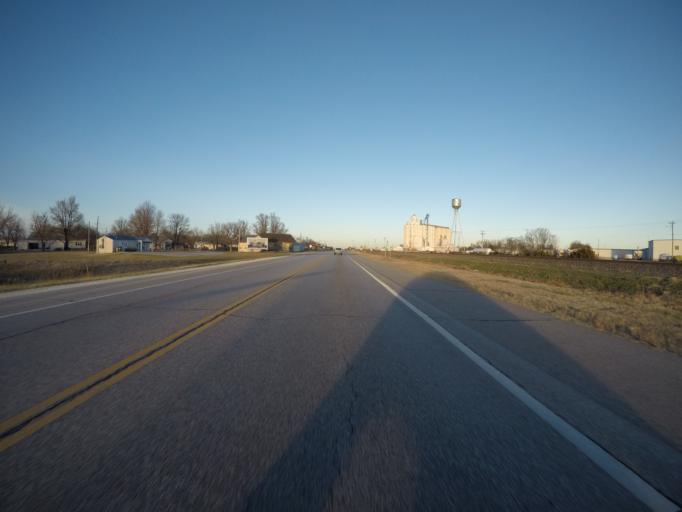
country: US
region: Kansas
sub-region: Harvey County
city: North Newton
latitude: 38.1155
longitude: -97.2584
